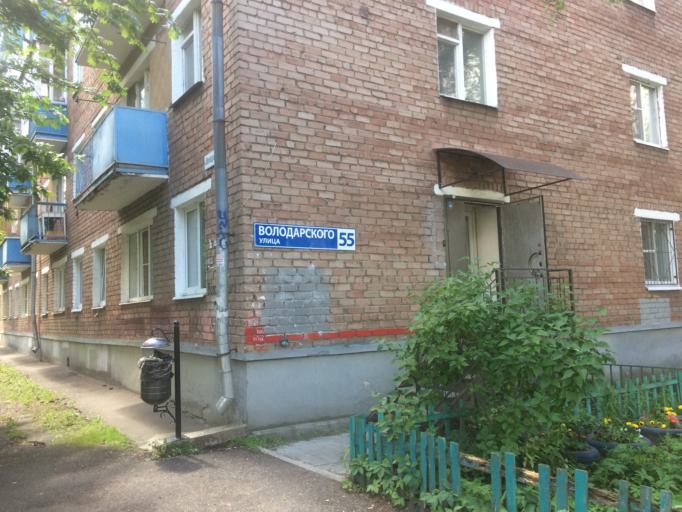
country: RU
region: Jaroslavl
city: Yaroslavl
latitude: 57.6290
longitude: 39.8630
